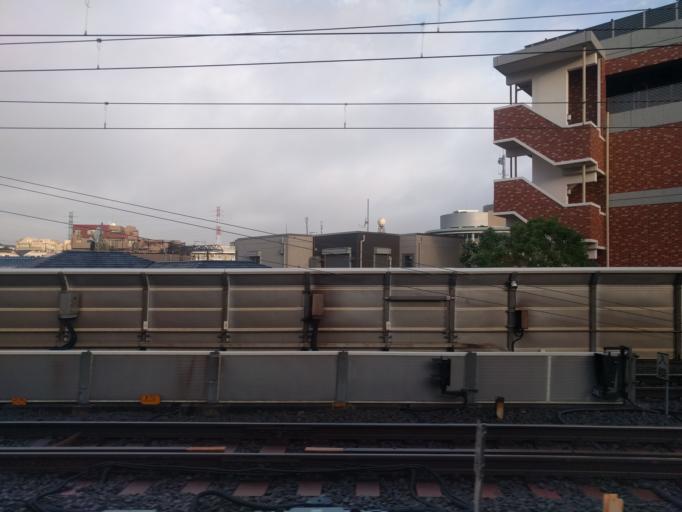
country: JP
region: Tokyo
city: Chofugaoka
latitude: 35.5985
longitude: 139.6089
